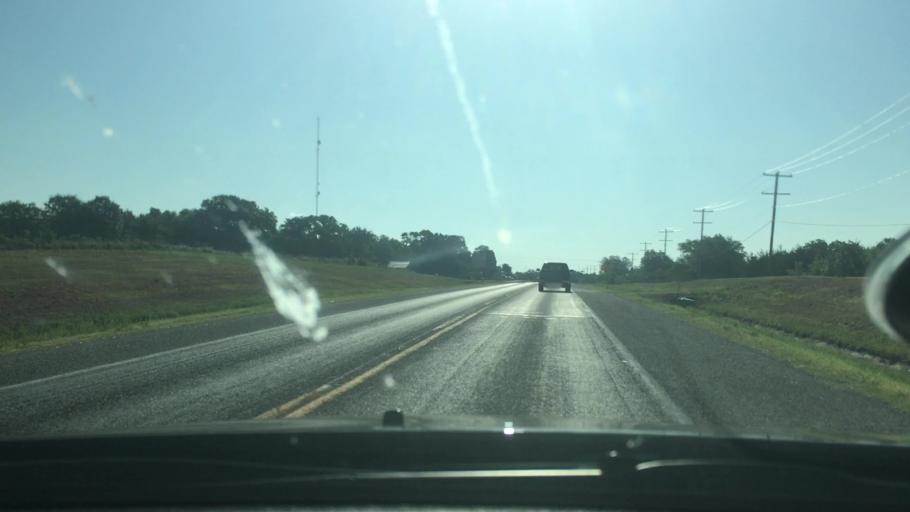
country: US
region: Oklahoma
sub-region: Johnston County
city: Tishomingo
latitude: 34.2370
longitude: -96.7082
